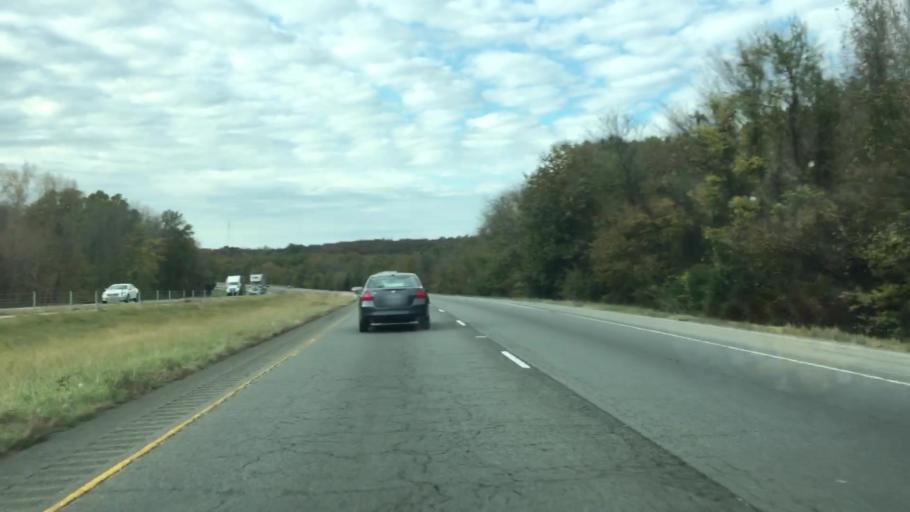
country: US
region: Arkansas
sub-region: Faulkner County
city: Conway
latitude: 35.1360
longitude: -92.5199
